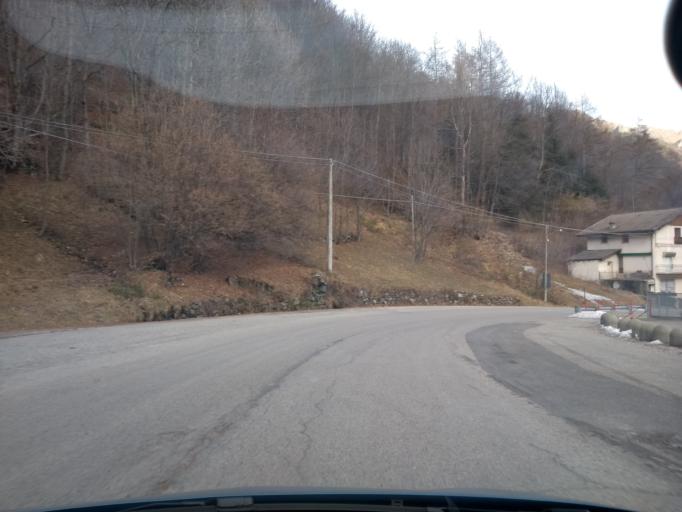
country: IT
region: Piedmont
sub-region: Provincia di Torino
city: Ala di Stura
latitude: 45.3142
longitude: 7.2723
